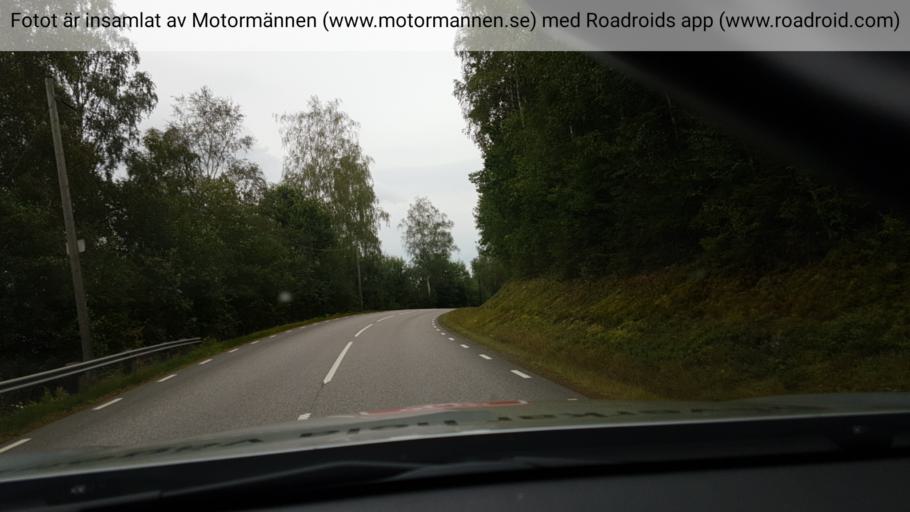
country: SE
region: Vaestra Goetaland
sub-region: Harryda Kommun
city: Hindas
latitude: 57.6094
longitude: 12.3565
